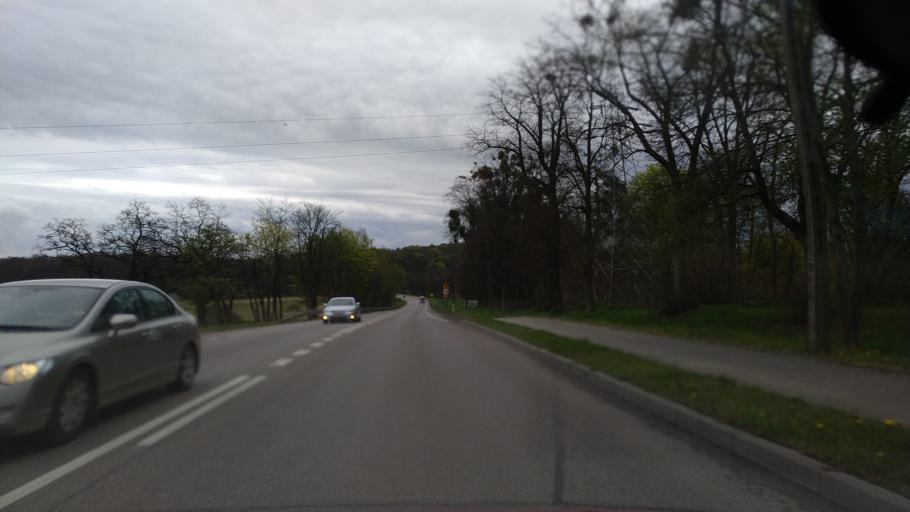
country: PL
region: Pomeranian Voivodeship
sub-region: Powiat starogardzki
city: Starogard Gdanski
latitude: 53.9717
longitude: 18.5467
